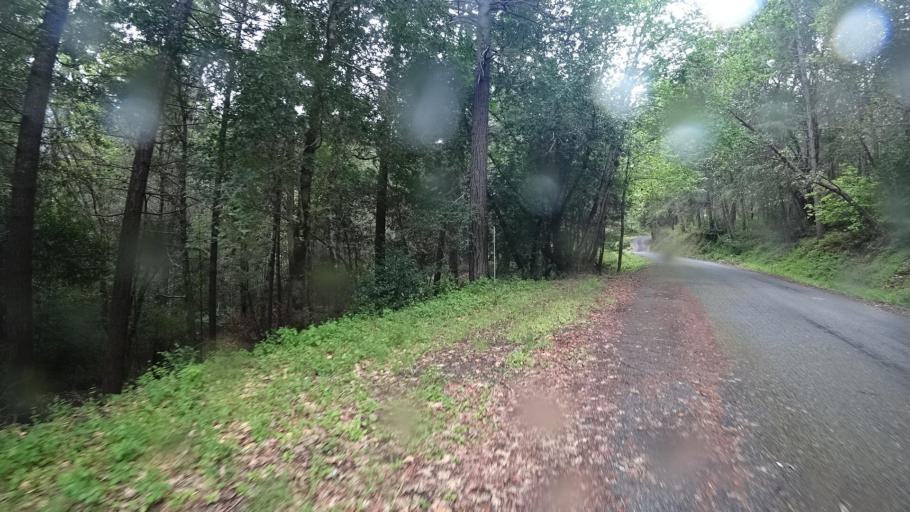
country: US
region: California
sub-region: Siskiyou County
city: Happy Camp
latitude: 41.3669
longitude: -123.5045
